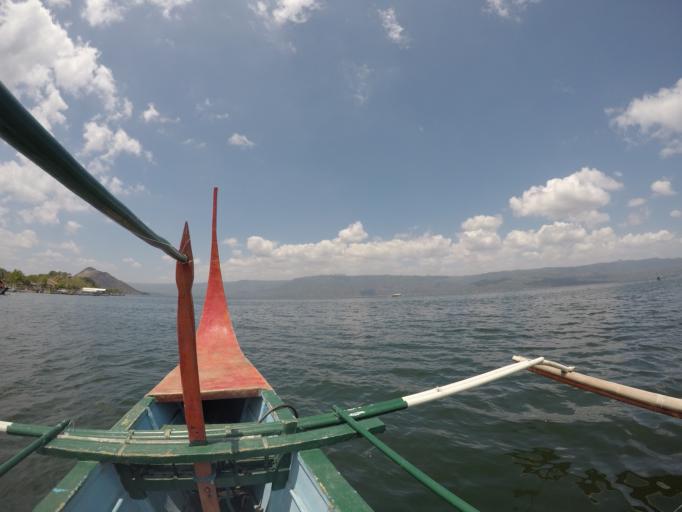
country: PH
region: Calabarzon
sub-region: Province of Batangas
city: Talisay
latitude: 14.0354
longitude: 121.0037
